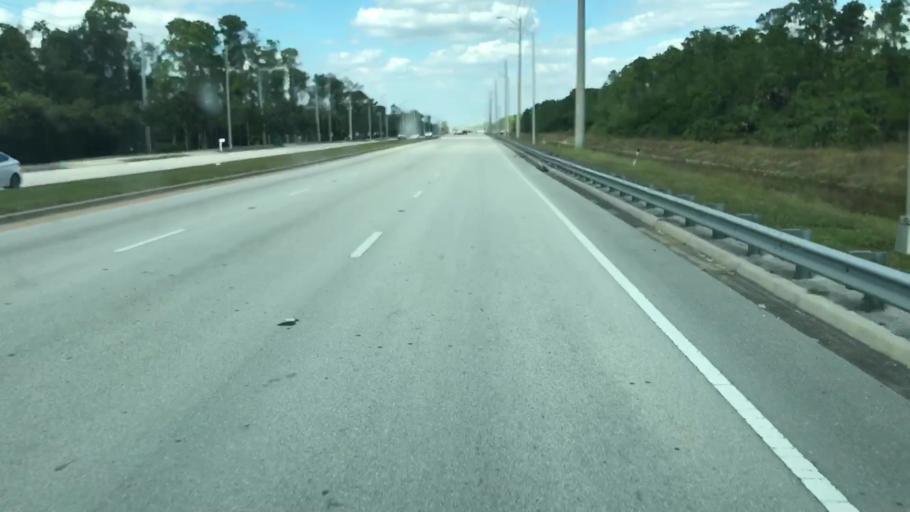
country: US
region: Florida
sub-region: Collier County
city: Vineyards
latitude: 26.2349
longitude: -81.6878
